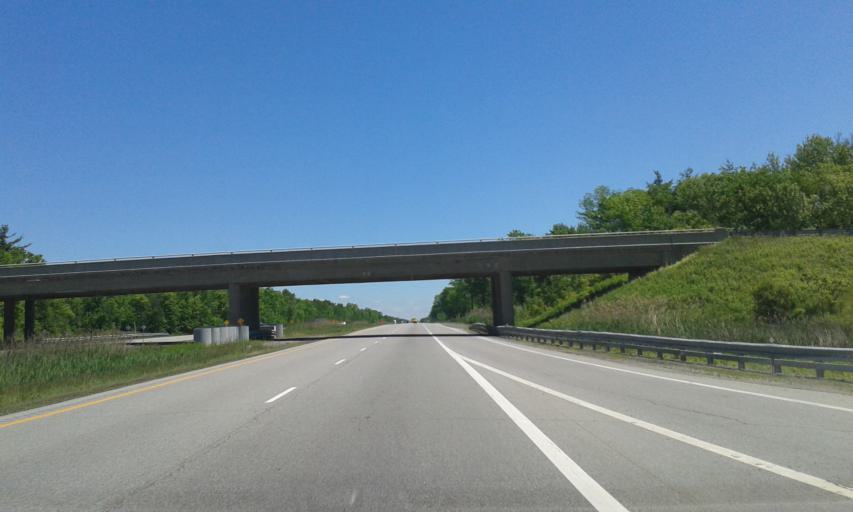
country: US
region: New York
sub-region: St. Lawrence County
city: Ogdensburg
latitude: 44.8100
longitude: -75.4060
